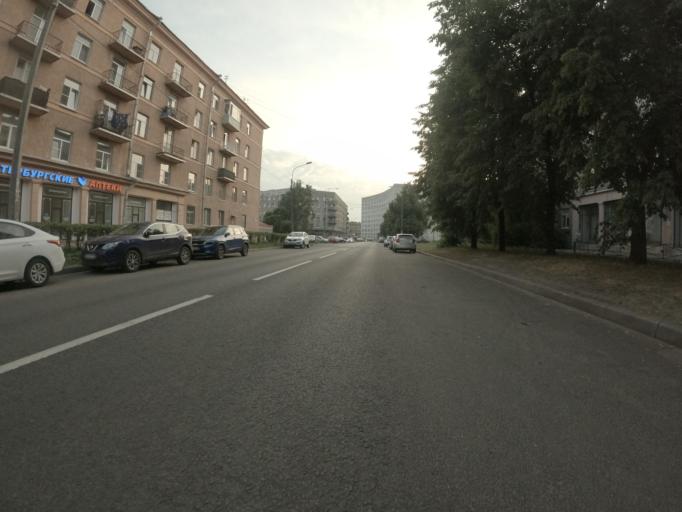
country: RU
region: Leningrad
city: Kalininskiy
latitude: 59.9707
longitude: 30.3906
